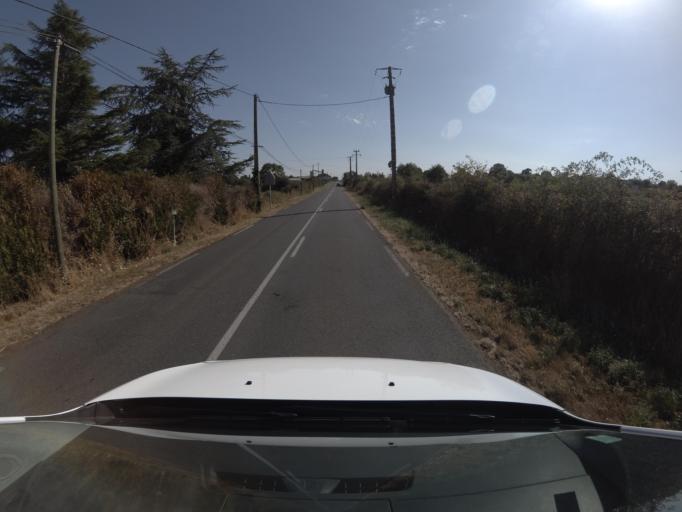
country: FR
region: Poitou-Charentes
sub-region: Departement des Deux-Sevres
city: Argenton-les-Vallees
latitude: 46.9958
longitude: -0.4320
